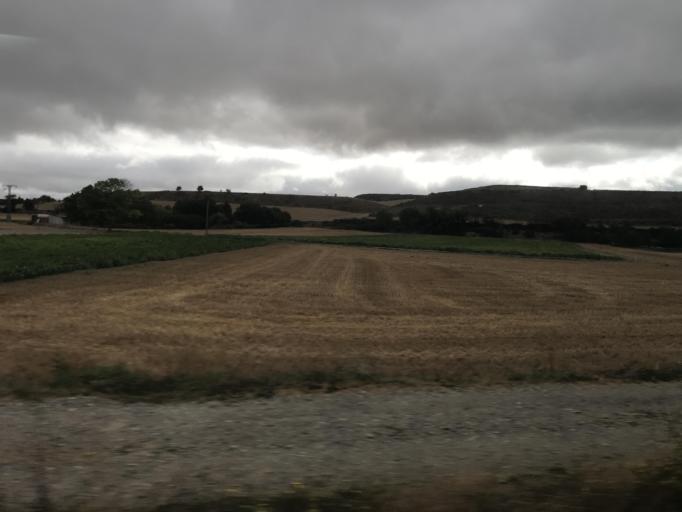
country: ES
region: Castille and Leon
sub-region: Provincia de Burgos
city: Miranda de Ebro
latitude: 42.6707
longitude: -2.9771
